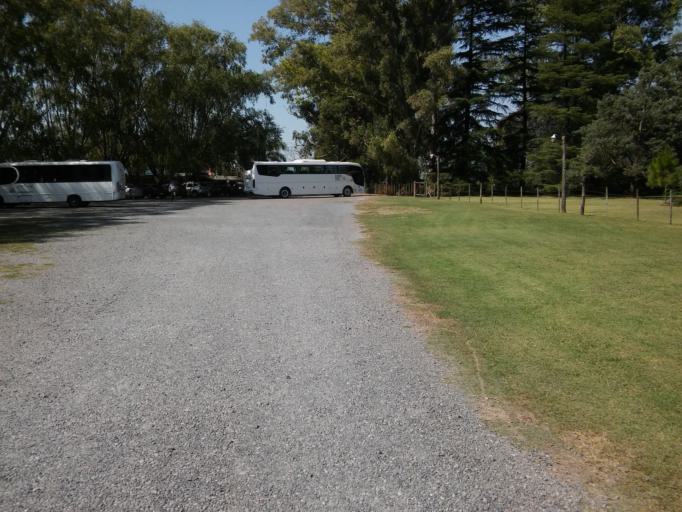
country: AR
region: Buenos Aires
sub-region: Partido de Campana
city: Campana
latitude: -34.2909
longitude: -58.9747
